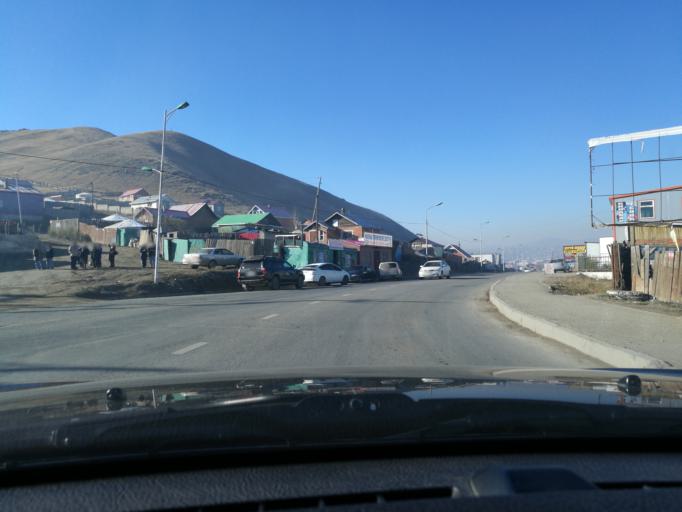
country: MN
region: Ulaanbaatar
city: Ulaanbaatar
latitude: 47.9780
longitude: 106.9389
